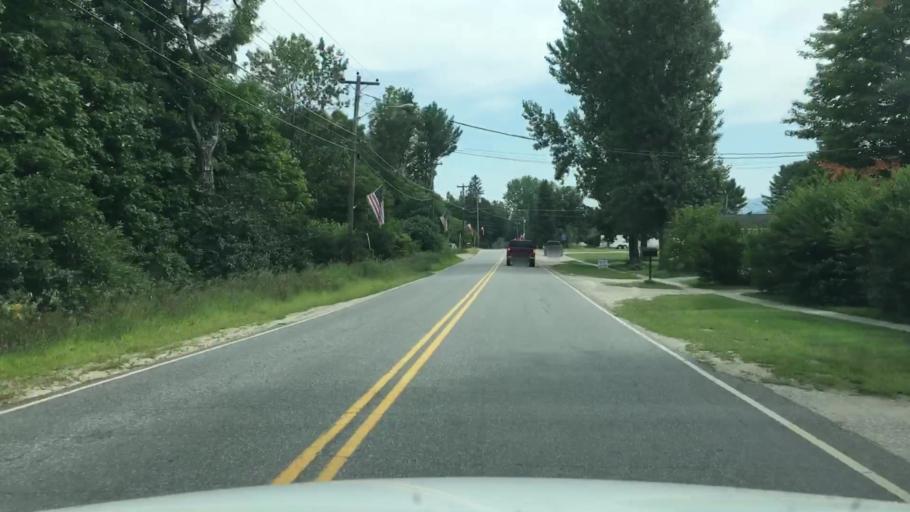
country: US
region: Maine
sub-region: Oxford County
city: Rumford
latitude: 44.6334
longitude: -70.7498
